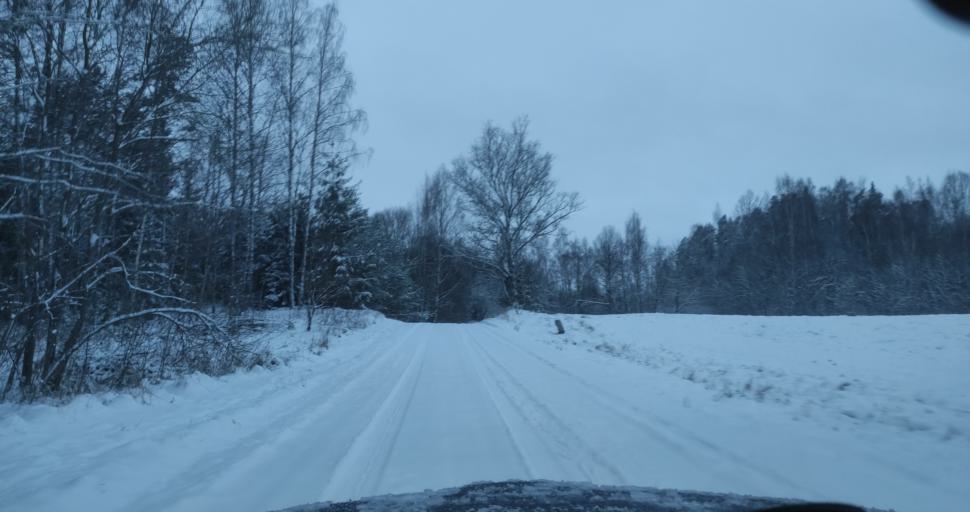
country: LV
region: Alsunga
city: Alsunga
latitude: 56.9506
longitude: 21.6282
